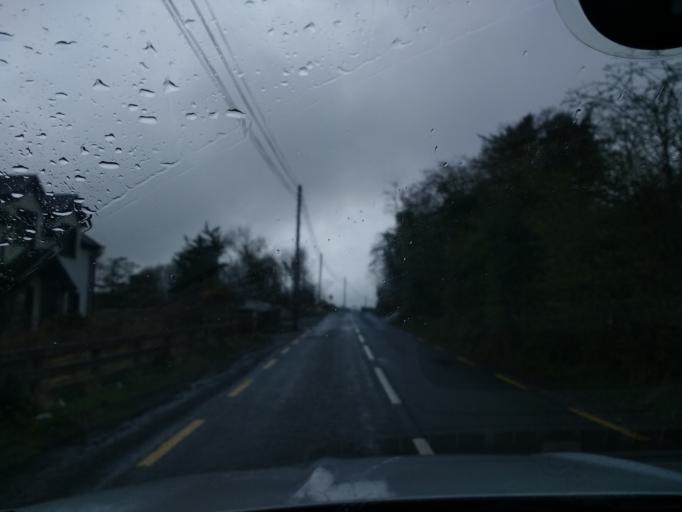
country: IE
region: Ulster
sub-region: County Donegal
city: Ramelton
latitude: 55.0747
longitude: -7.5959
